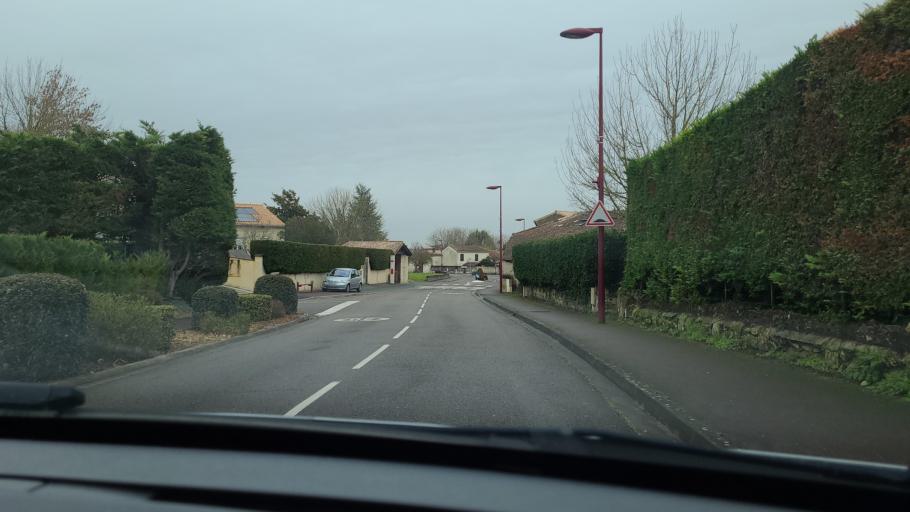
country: FR
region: Aquitaine
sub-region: Departement de la Gironde
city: Pugnac
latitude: 45.0826
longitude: -0.4922
